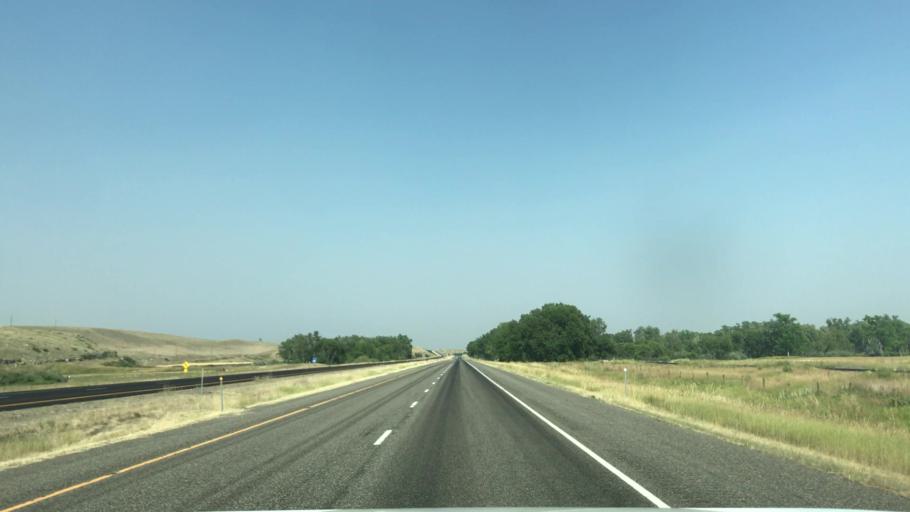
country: US
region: Montana
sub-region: Cascade County
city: Sun Prairie
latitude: 47.2329
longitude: -111.7502
